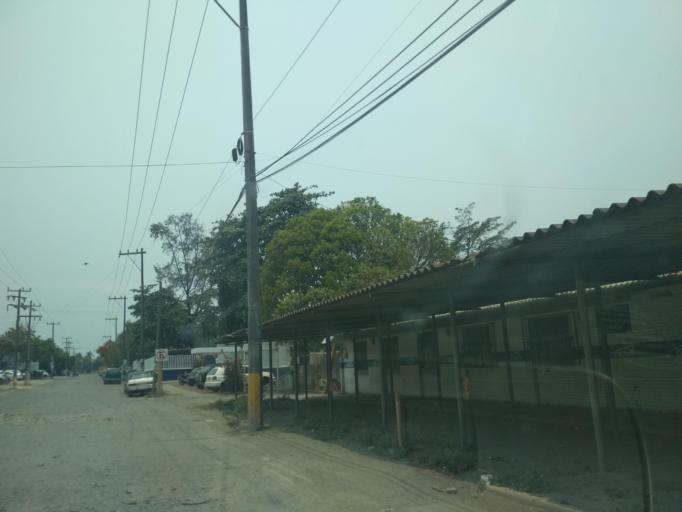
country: MX
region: Veracruz
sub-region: Veracruz
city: Lomas de Rio Medio Cuatro
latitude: 19.1697
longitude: -96.2343
